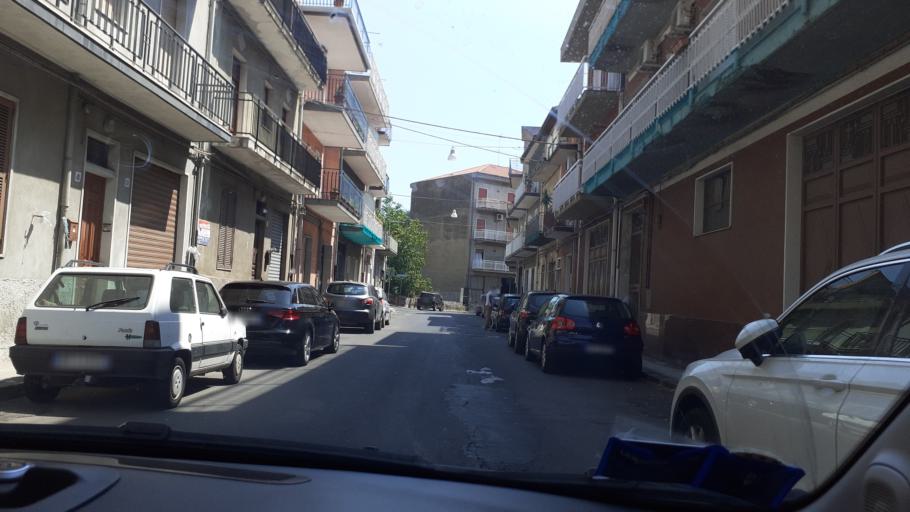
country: IT
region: Sicily
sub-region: Catania
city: Misterbianco
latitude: 37.5172
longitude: 15.0172
